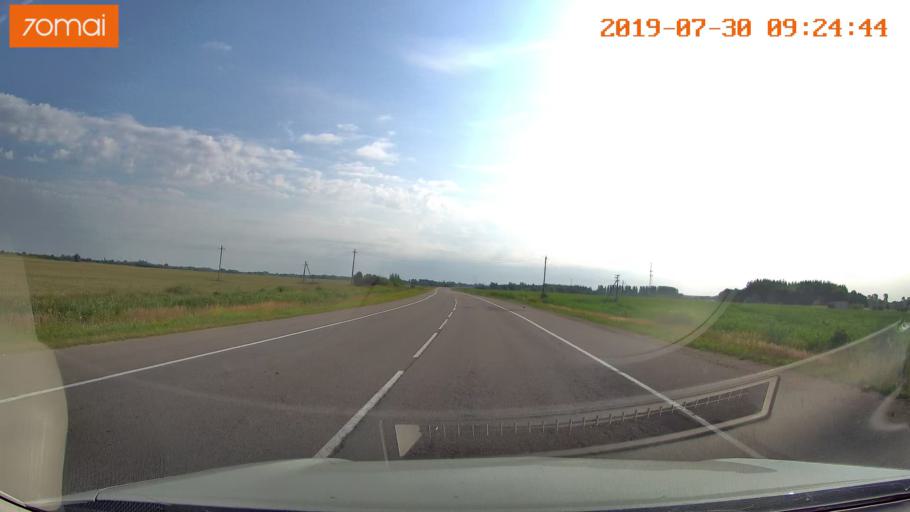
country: LT
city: Kybartai
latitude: 54.6344
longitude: 22.7014
